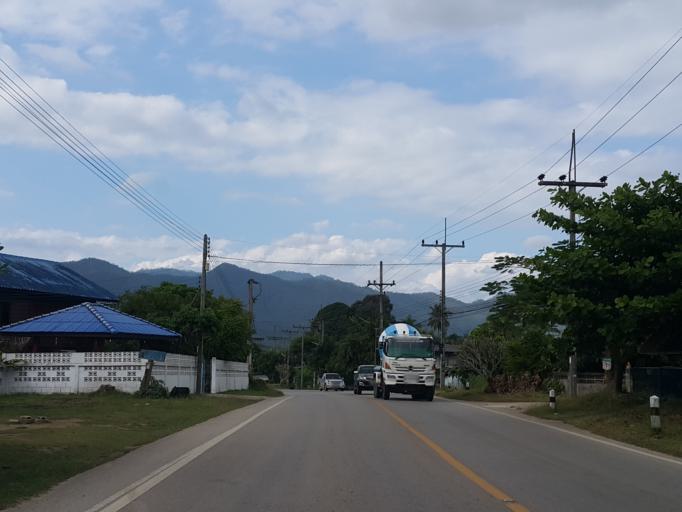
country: TH
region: Lampang
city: Chae Hom
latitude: 18.5717
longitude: 99.4707
